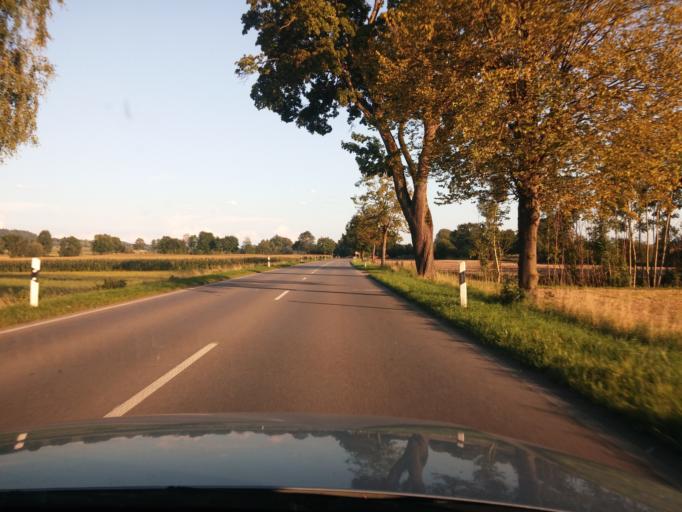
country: DE
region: Baden-Wuerttemberg
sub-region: Tuebingen Region
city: Salem
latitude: 47.7535
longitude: 9.3159
